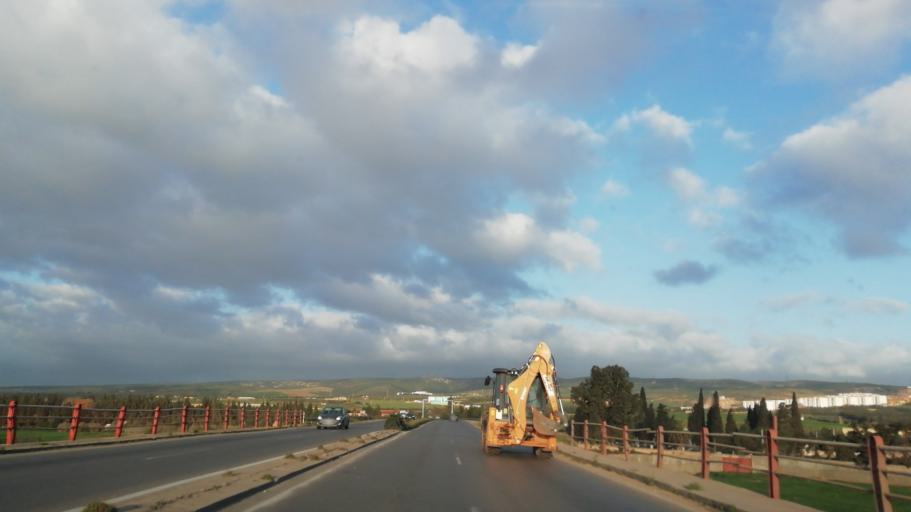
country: DZ
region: Oran
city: Es Senia
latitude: 35.6065
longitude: -0.7417
